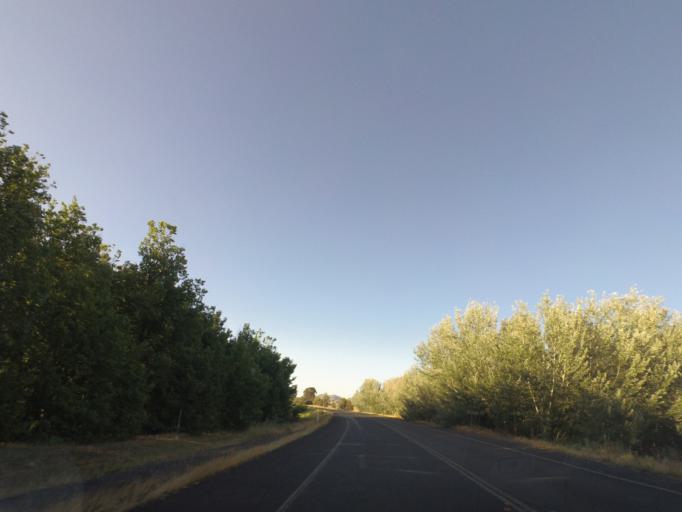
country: AU
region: New South Wales
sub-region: Gundagai
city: Gundagai
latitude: -34.9464
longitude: 148.1689
